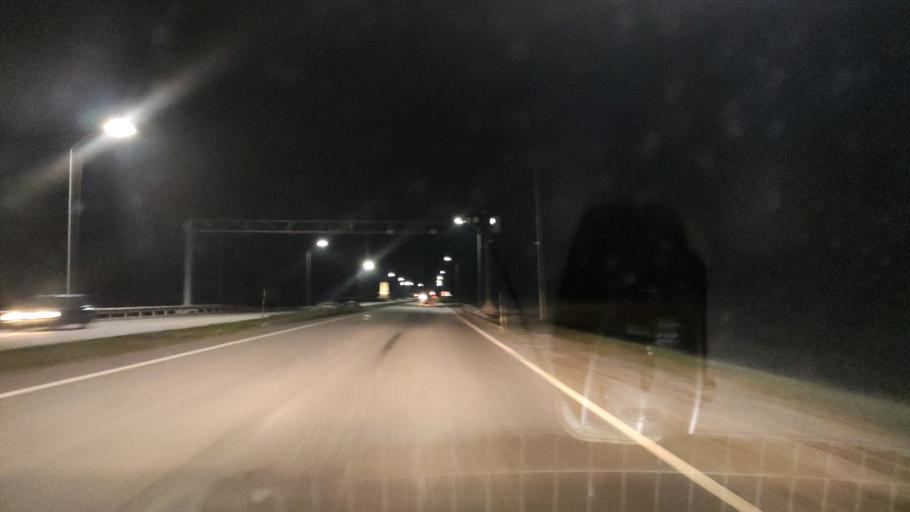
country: RU
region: Belgorod
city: Staryy Oskol
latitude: 51.4238
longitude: 37.8940
